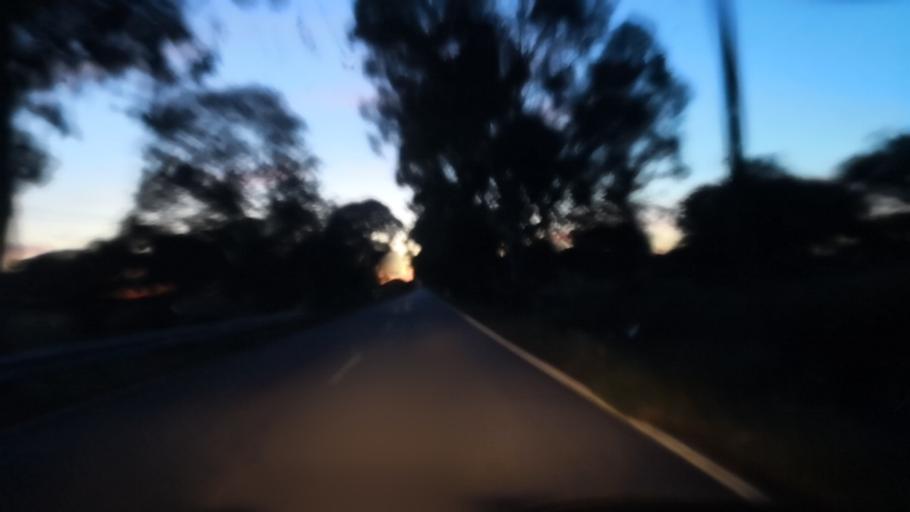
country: ES
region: Extremadura
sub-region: Provincia de Caceres
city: Piedras Albas
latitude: 39.8624
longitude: -7.0082
